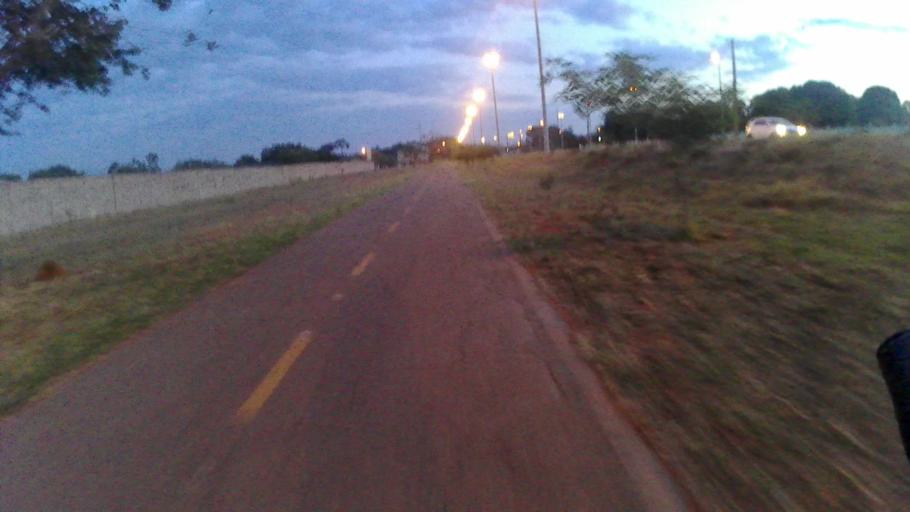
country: BR
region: Federal District
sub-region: Brasilia
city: Brasilia
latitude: -15.8709
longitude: -47.9908
